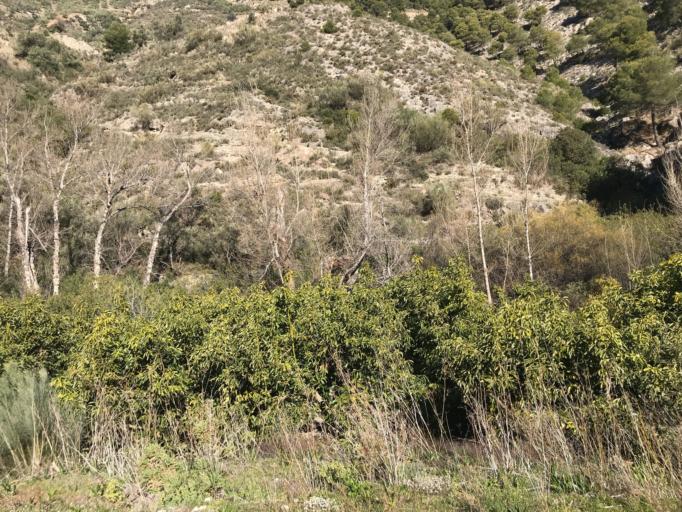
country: ES
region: Andalusia
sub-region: Provincia de Malaga
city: Canillas de Albaida
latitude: 36.8510
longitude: -3.9847
